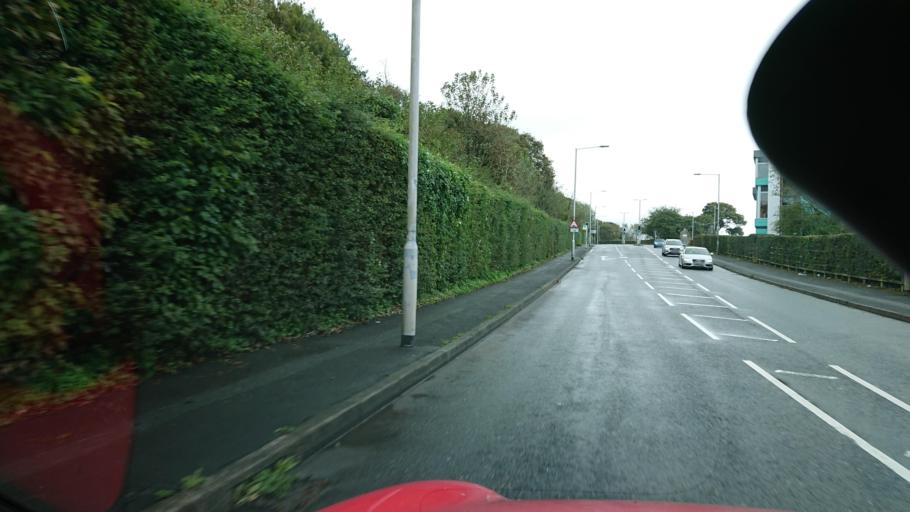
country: GB
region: England
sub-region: Plymouth
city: Plymouth
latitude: 50.4180
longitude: -4.1122
